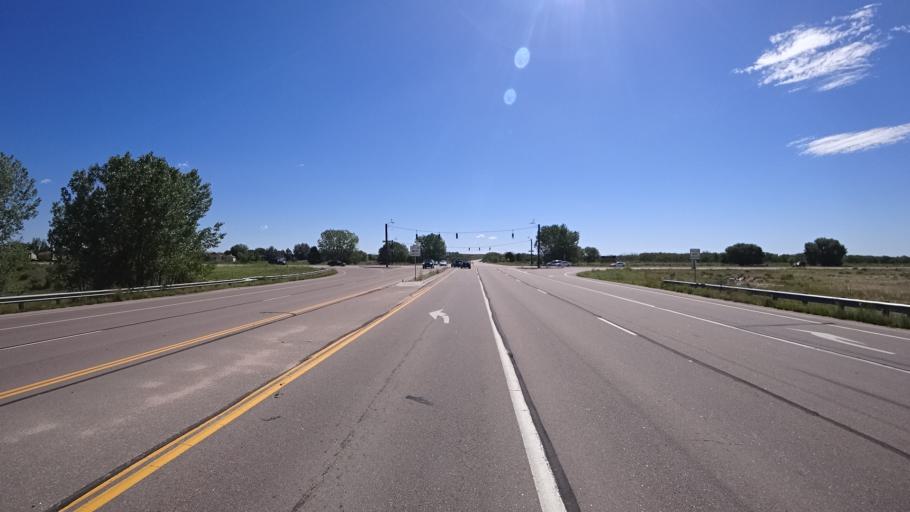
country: US
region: Colorado
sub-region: El Paso County
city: Security-Widefield
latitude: 38.7621
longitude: -104.6607
